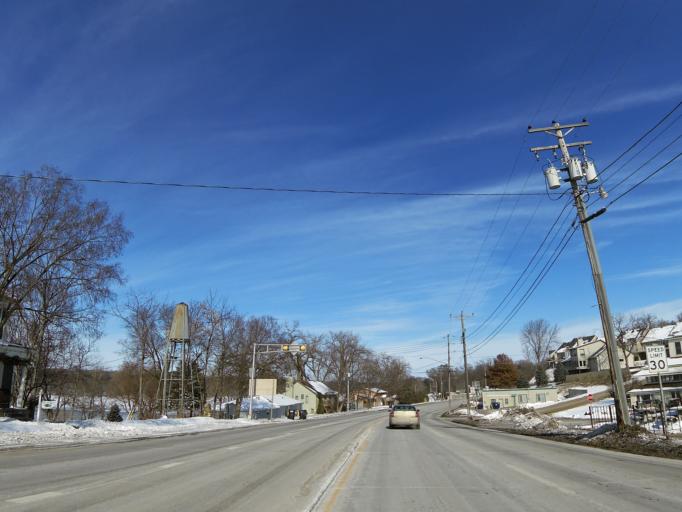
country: US
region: Wisconsin
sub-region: Pierce County
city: Prescott
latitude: 44.7505
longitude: -92.8033
